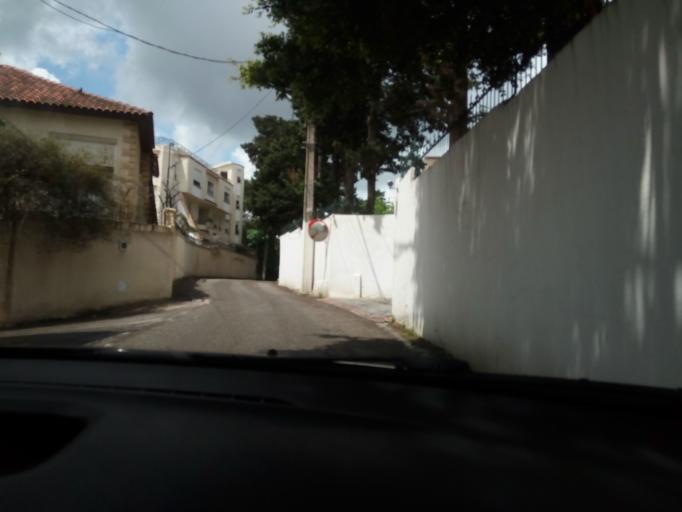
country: DZ
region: Alger
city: Algiers
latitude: 36.7644
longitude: 3.0345
